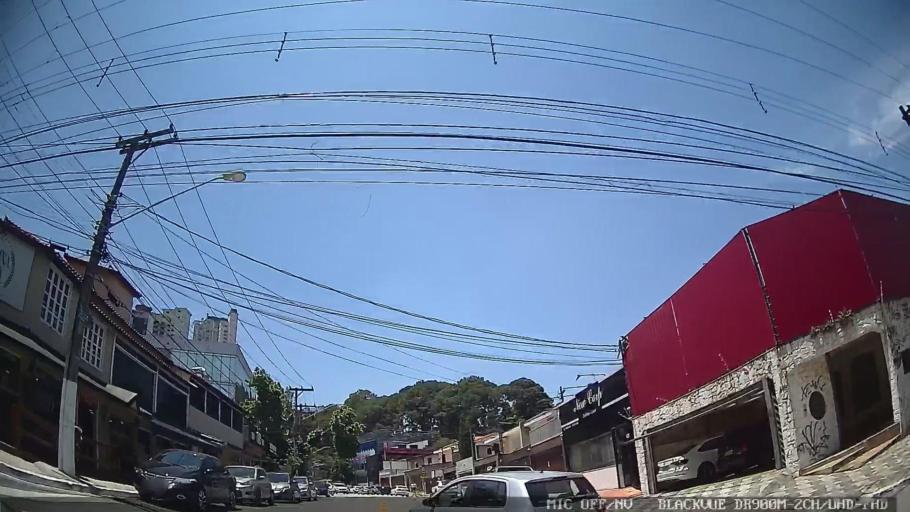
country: BR
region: Sao Paulo
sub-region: Sao Caetano Do Sul
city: Sao Caetano do Sul
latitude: -23.5598
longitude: -46.5662
